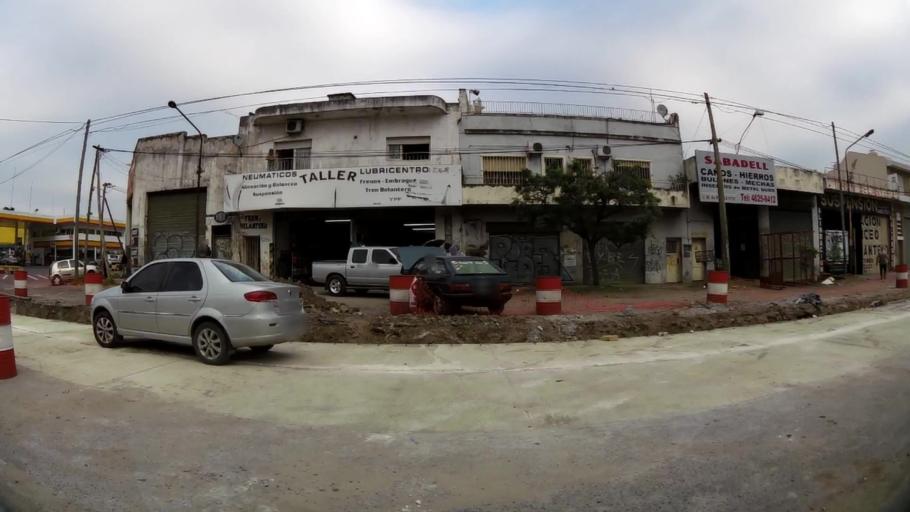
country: AR
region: Buenos Aires
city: San Justo
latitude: -34.6988
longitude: -58.5778
